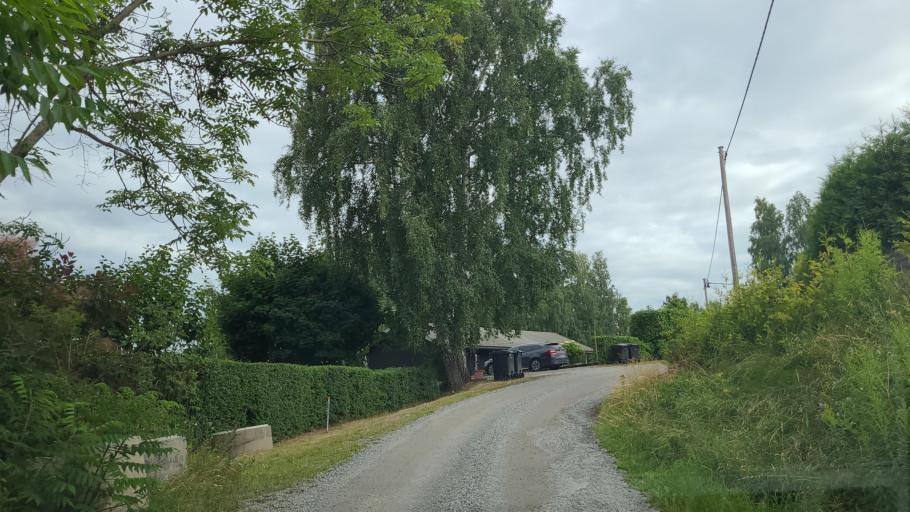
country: SE
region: Stockholm
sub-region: Upplands-Bro Kommun
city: Bro
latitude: 59.4767
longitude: 17.5578
